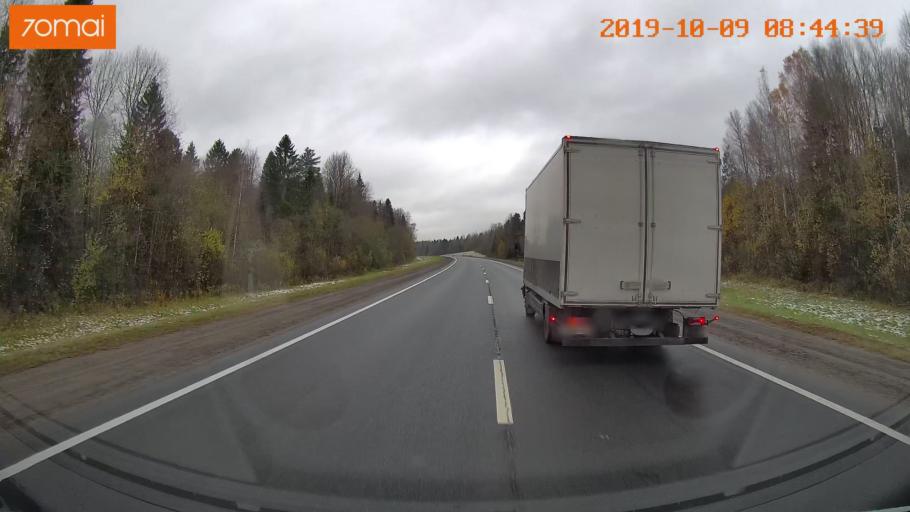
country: RU
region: Vologda
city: Gryazovets
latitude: 59.0391
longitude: 40.1058
